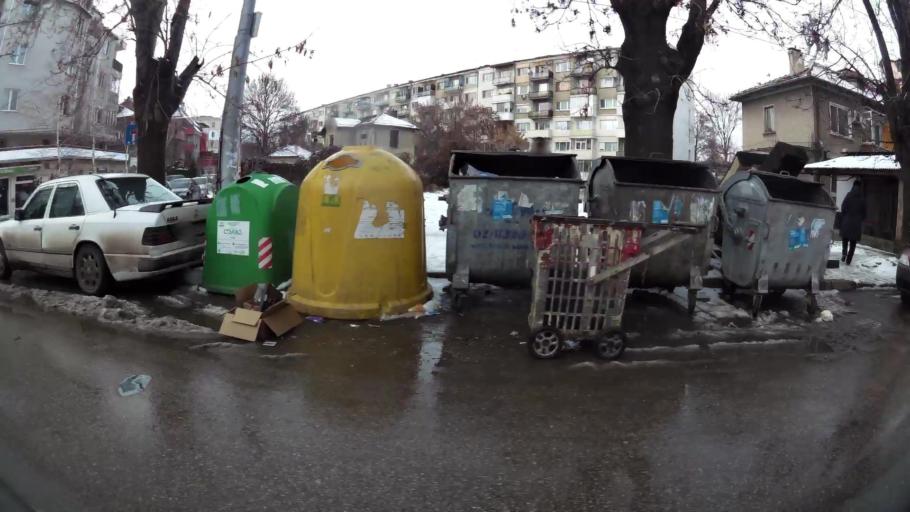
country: BG
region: Sofia-Capital
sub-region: Stolichna Obshtina
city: Sofia
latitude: 42.7098
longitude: 23.3487
